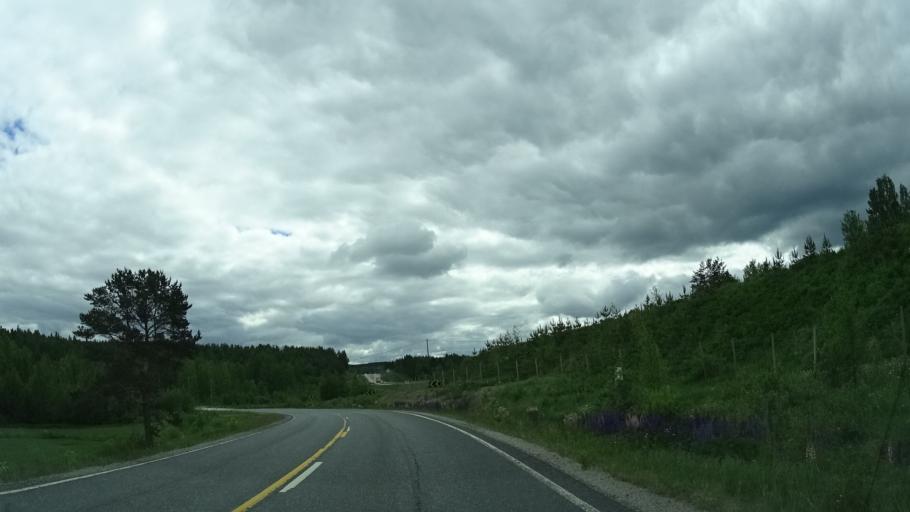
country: FI
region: Central Finland
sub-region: Jyvaeskylae
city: Toivakka
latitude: 62.0788
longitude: 26.0348
